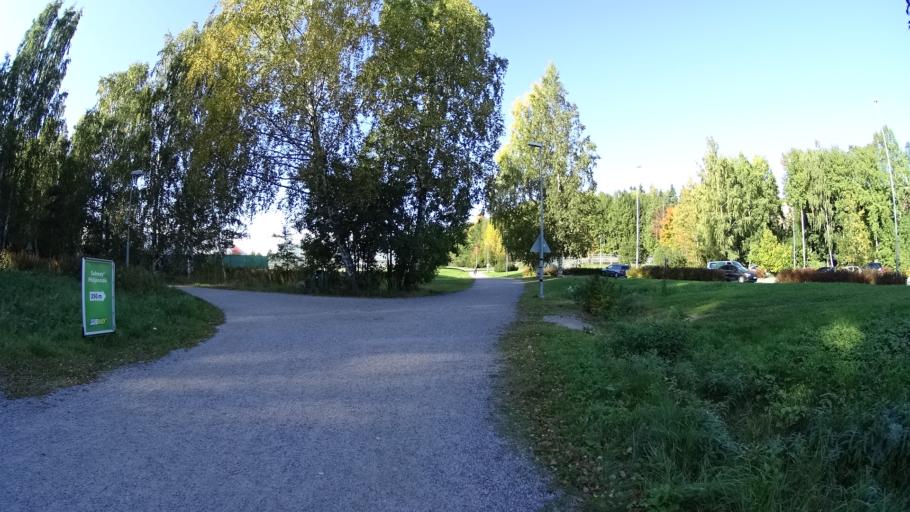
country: FI
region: Uusimaa
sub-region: Helsinki
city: Teekkarikylae
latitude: 60.2114
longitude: 24.8777
